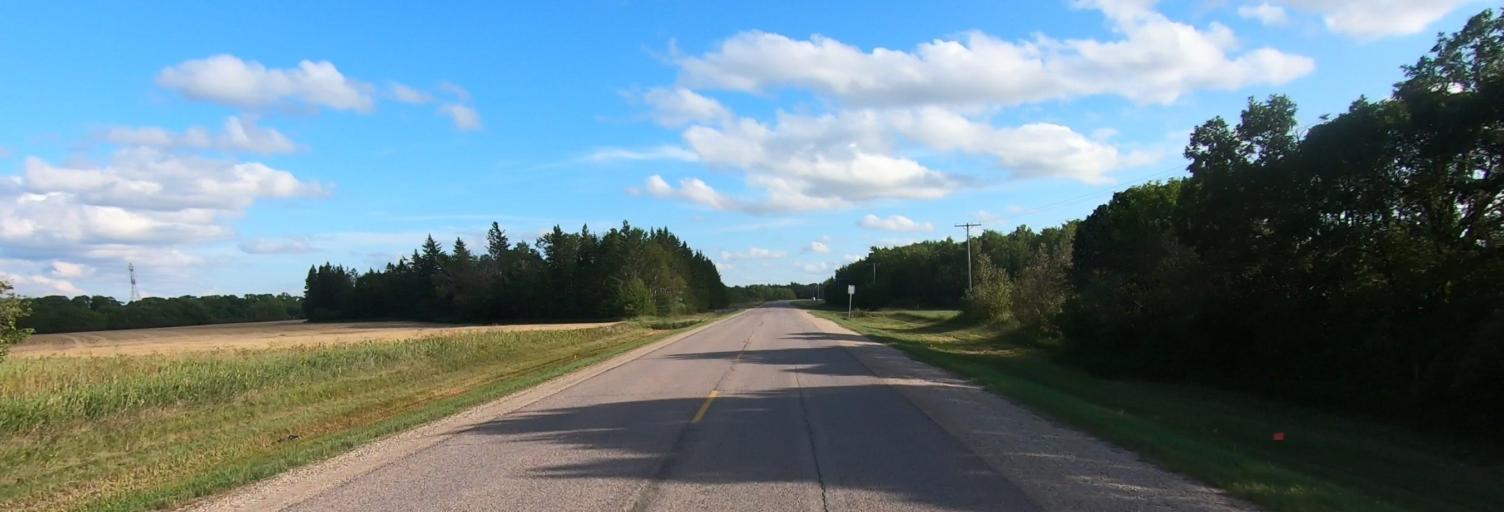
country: CA
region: Manitoba
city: Selkirk
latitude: 50.2074
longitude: -96.8402
